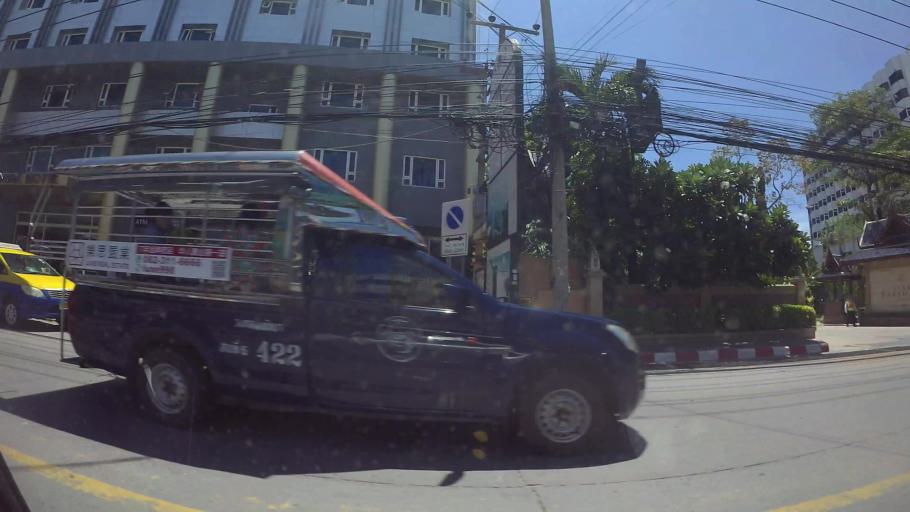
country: TH
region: Chon Buri
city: Phatthaya
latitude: 12.9227
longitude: 100.8717
